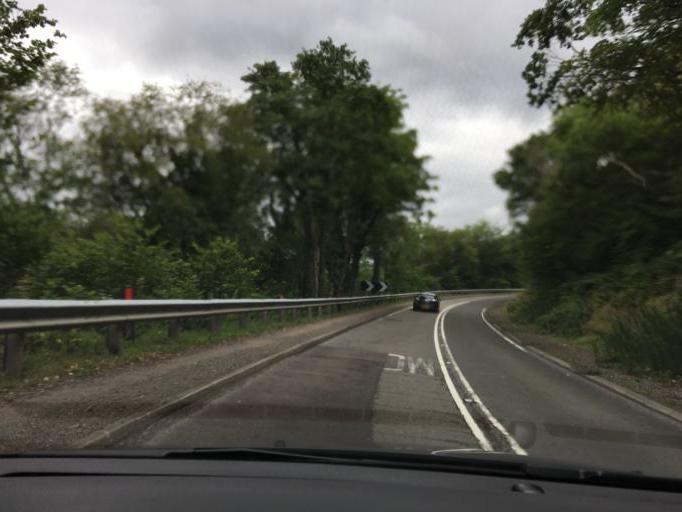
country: GB
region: Scotland
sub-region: Highland
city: Fort William
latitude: 56.7817
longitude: -5.1624
